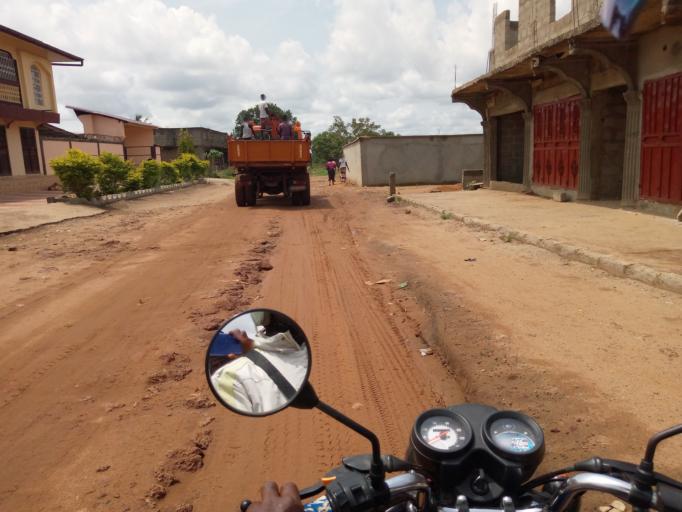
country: SL
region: Western Area
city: Waterloo
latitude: 8.3595
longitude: -13.0717
